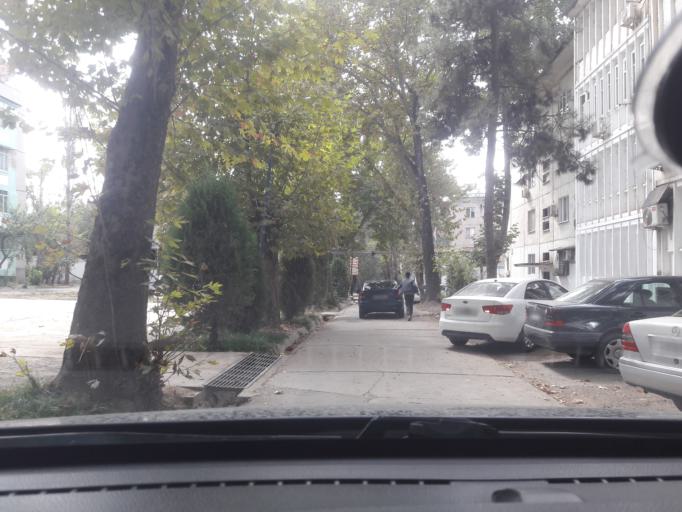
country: TJ
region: Dushanbe
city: Dushanbe
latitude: 38.5878
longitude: 68.7500
